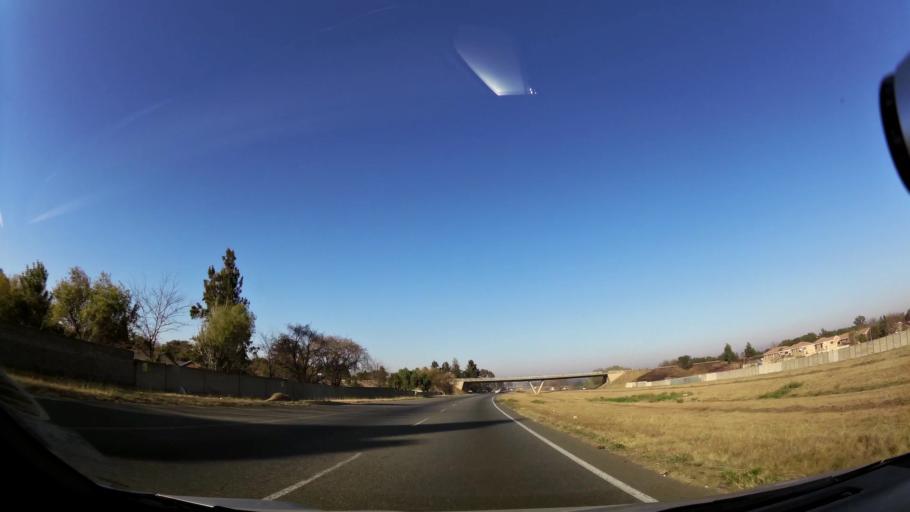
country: ZA
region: Gauteng
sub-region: Ekurhuleni Metropolitan Municipality
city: Germiston
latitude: -26.3292
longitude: 28.1118
